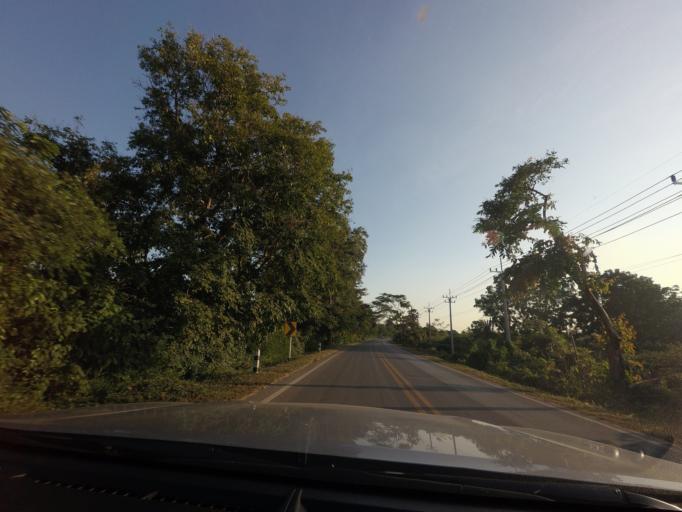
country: TH
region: Sukhothai
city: Sawankhalok
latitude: 17.3400
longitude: 99.8270
